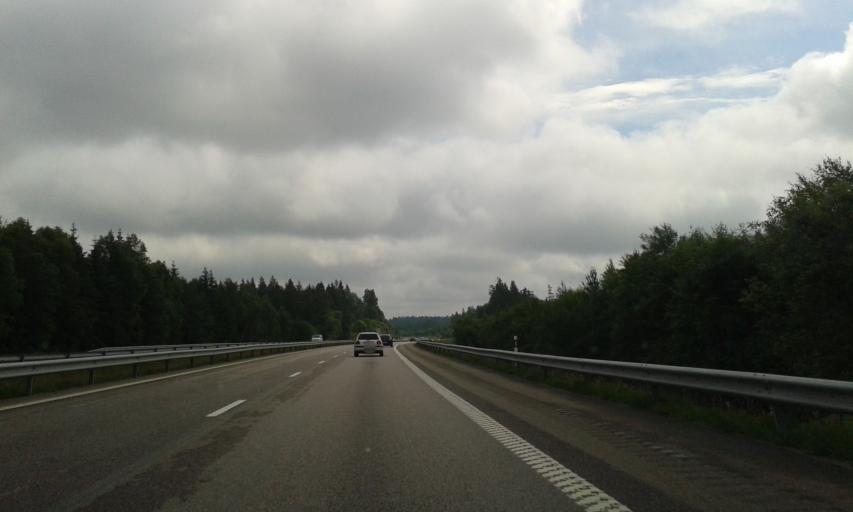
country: SE
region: Vaestra Goetaland
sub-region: Bollebygds Kommun
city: Bollebygd
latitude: 57.6750
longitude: 12.6810
